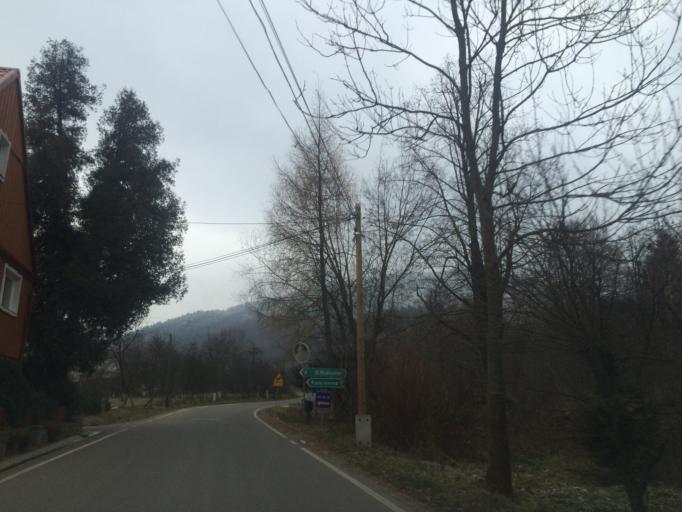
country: PL
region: Lower Silesian Voivodeship
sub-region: Powiat klodzki
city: Bystrzyca Klodzka
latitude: 50.2676
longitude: 16.7500
